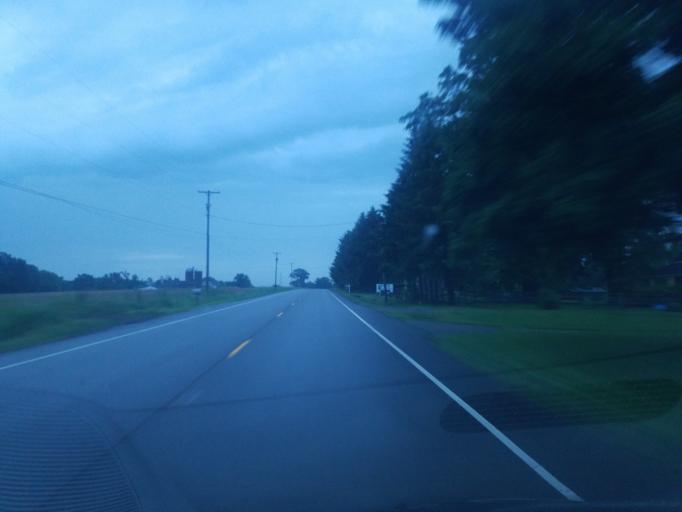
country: US
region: Ohio
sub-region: Mahoning County
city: Canfield
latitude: 40.9853
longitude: -80.7582
